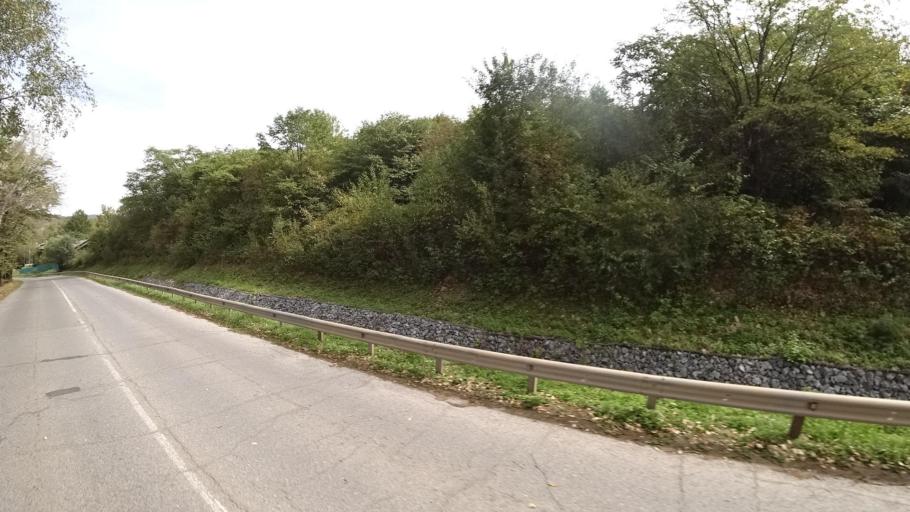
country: RU
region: Jewish Autonomous Oblast
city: Khingansk
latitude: 49.0068
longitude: 131.0602
